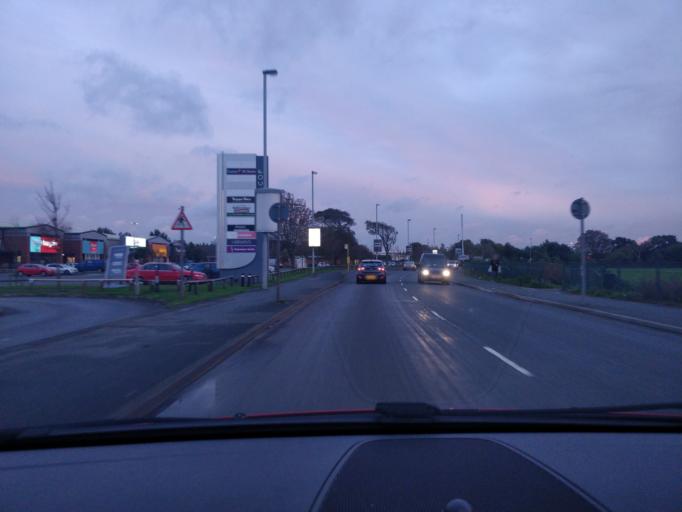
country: GB
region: England
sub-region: Sefton
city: Southport
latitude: 53.6360
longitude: -2.9709
